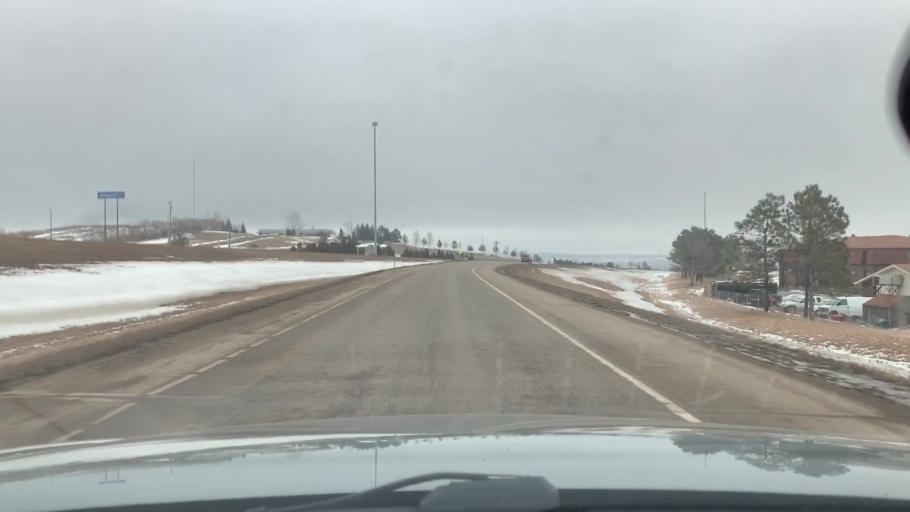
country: US
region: North Dakota
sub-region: Morton County
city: Mandan
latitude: 46.8439
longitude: -100.9055
